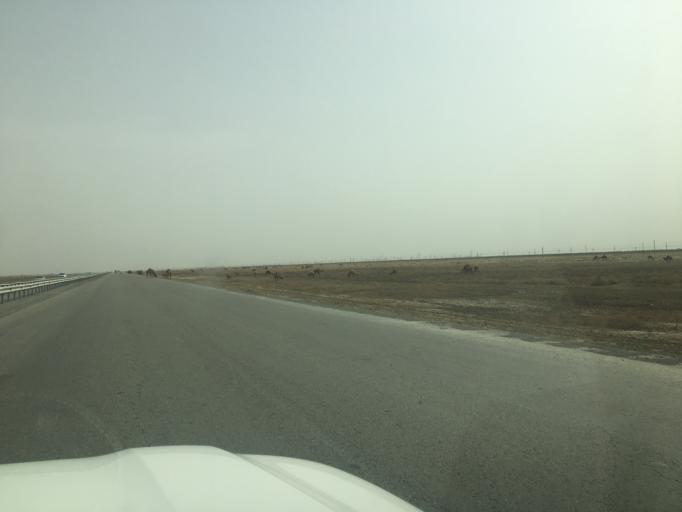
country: TM
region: Ahal
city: Tejen
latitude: 37.3354
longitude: 60.3783
